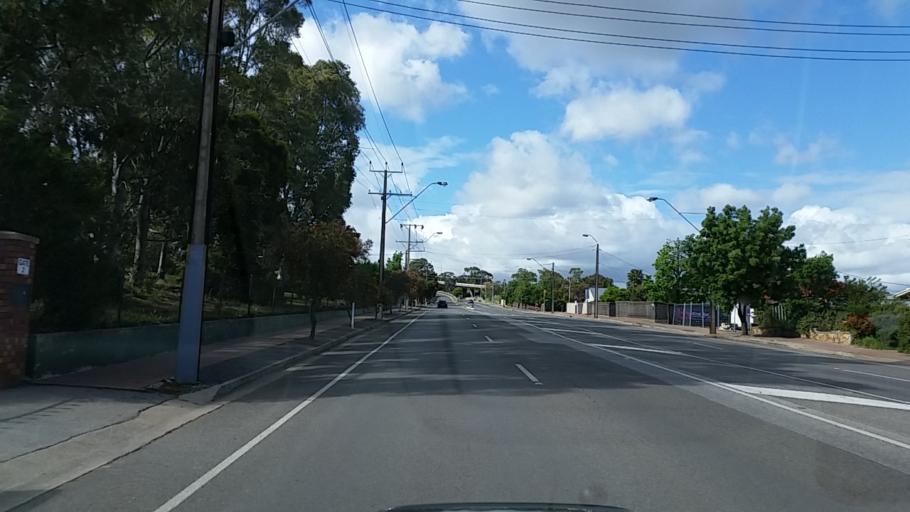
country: AU
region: South Australia
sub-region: Marion
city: Marion
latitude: -35.0138
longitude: 138.5765
